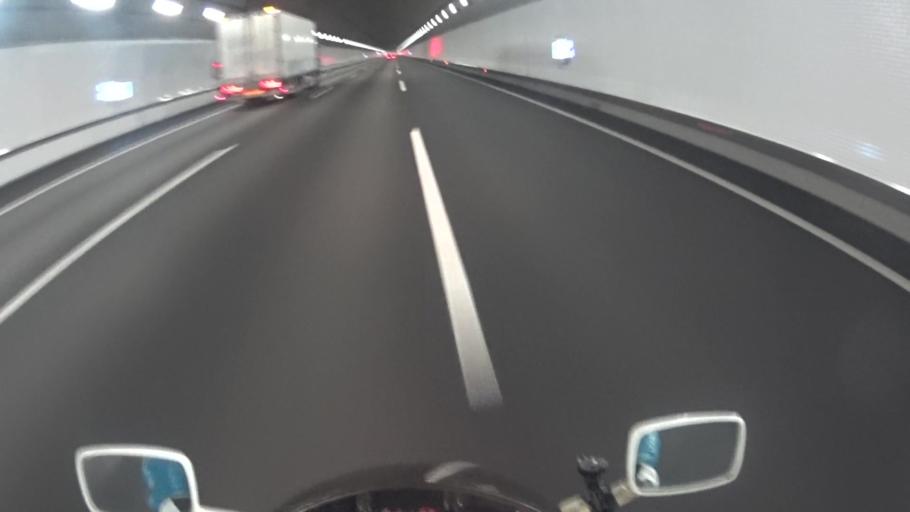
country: JP
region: Mie
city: Kameyama
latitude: 34.9154
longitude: 136.3741
